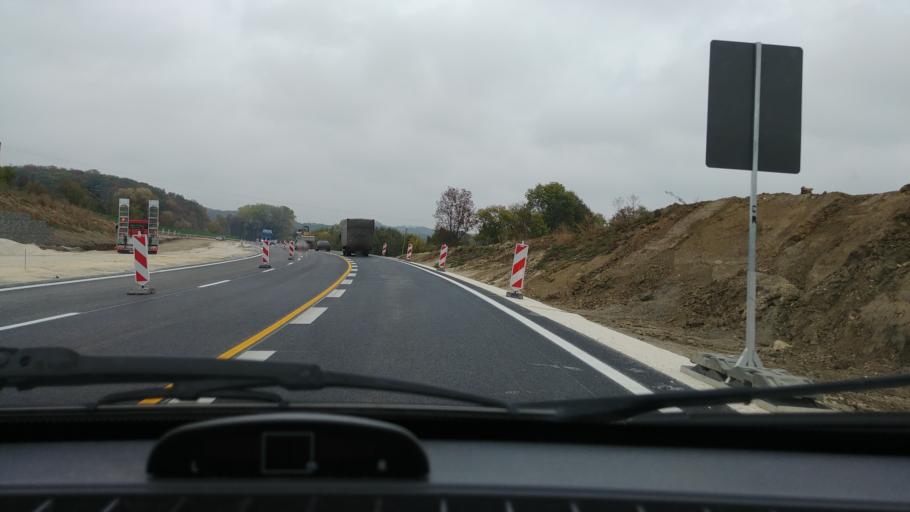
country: DE
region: Baden-Wuerttemberg
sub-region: Regierungsbezirk Stuttgart
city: Mogglingen
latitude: 48.8217
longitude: 9.9935
